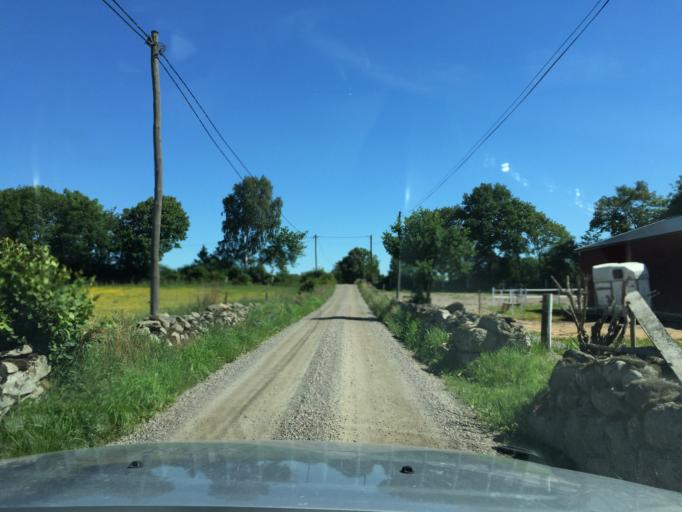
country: SE
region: Skane
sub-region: Hassleholms Kommun
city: Sosdala
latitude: 56.0210
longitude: 13.6427
